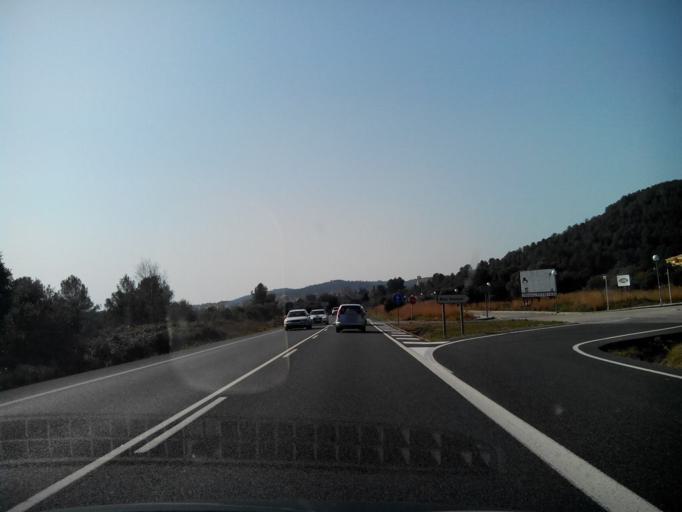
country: ES
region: Catalonia
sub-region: Provincia de Tarragona
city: Alcover
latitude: 41.2745
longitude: 1.1784
